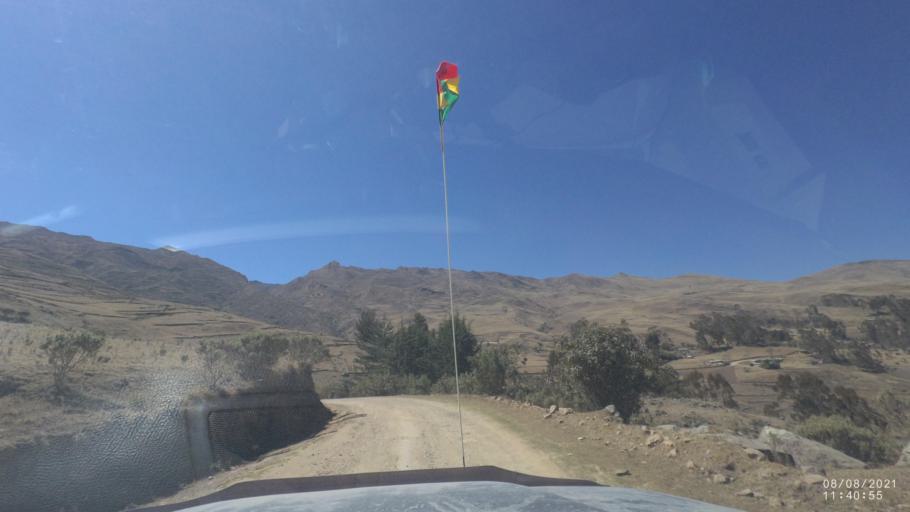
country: BO
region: Cochabamba
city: Colchani
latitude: -16.7961
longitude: -66.6448
